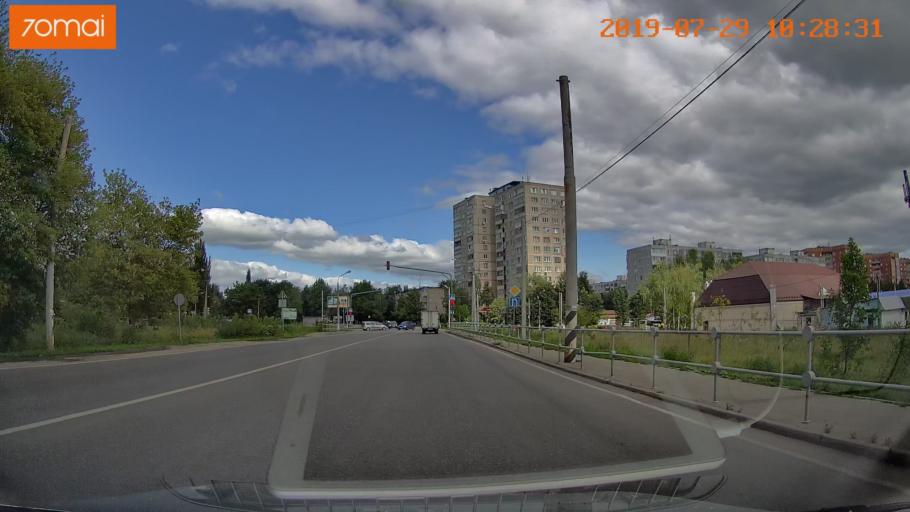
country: RU
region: Moskovskaya
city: Voskresensk
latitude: 55.3127
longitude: 38.6542
